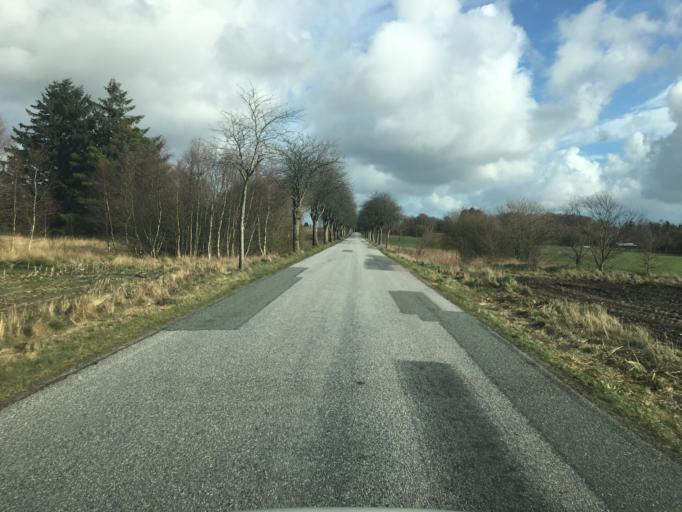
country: DK
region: South Denmark
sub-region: Aabenraa Kommune
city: Krusa
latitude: 54.9014
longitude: 9.3992
